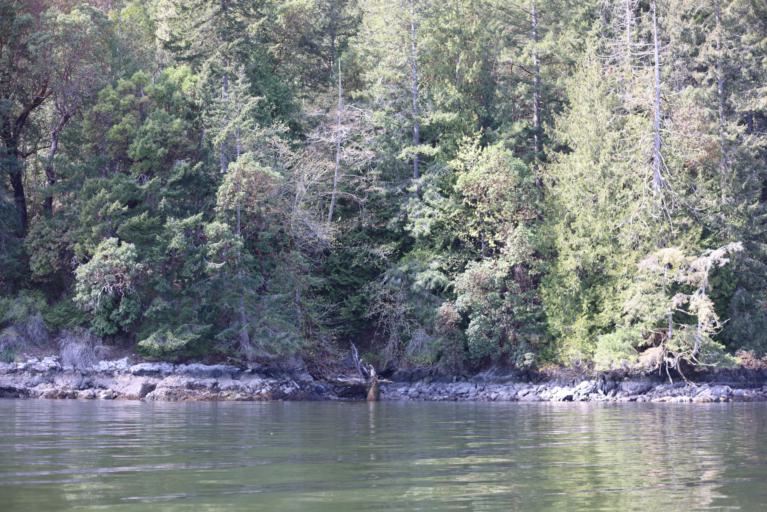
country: CA
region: British Columbia
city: North Saanich
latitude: 48.5919
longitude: -123.5207
